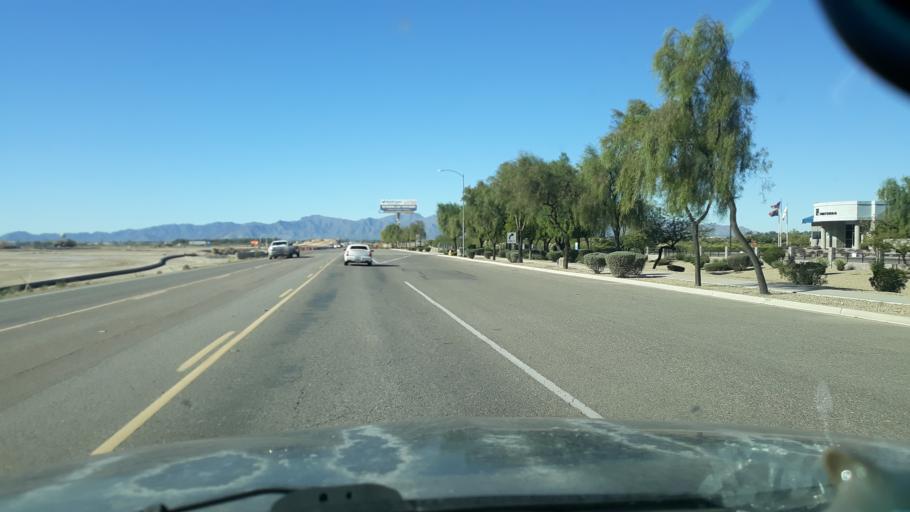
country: US
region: Arizona
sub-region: Maricopa County
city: Youngtown
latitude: 33.5512
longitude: -112.3303
